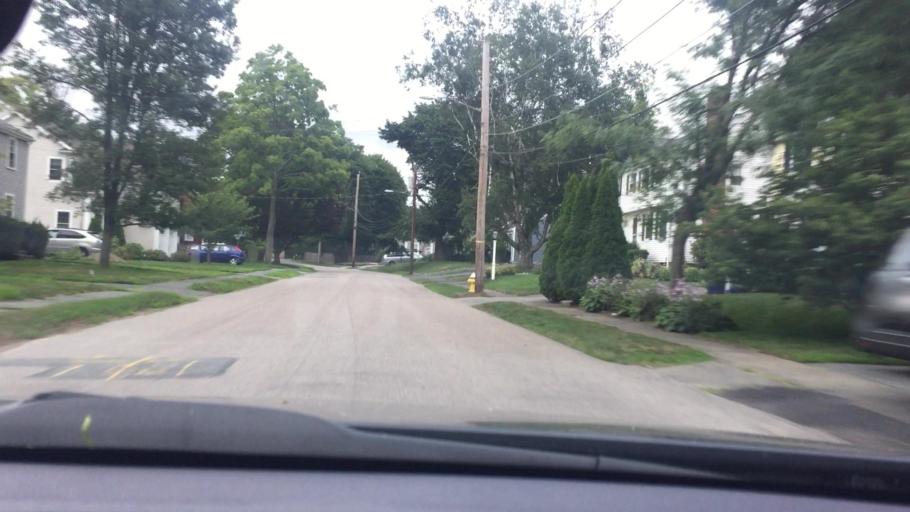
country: US
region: Massachusetts
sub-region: Norfolk County
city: Needham
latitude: 42.2895
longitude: -71.2337
